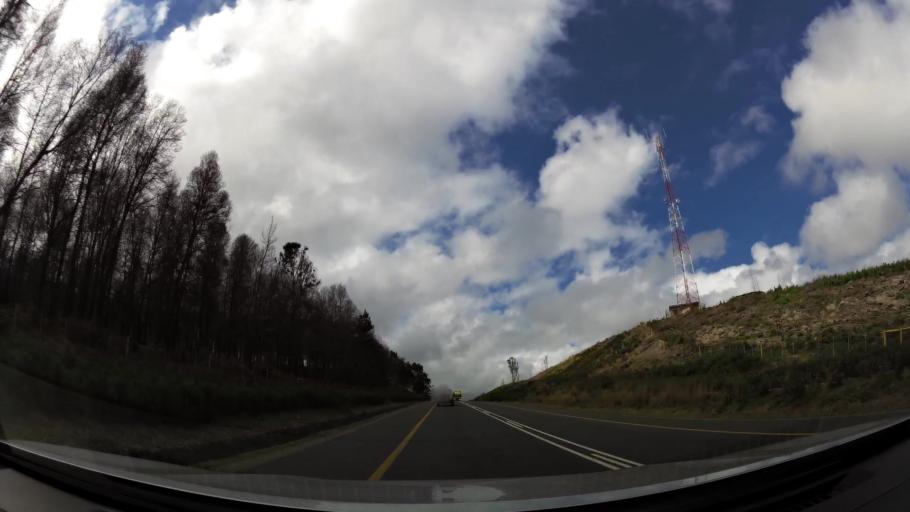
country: ZA
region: Western Cape
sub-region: Eden District Municipality
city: Knysna
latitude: -34.0372
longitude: 23.1450
